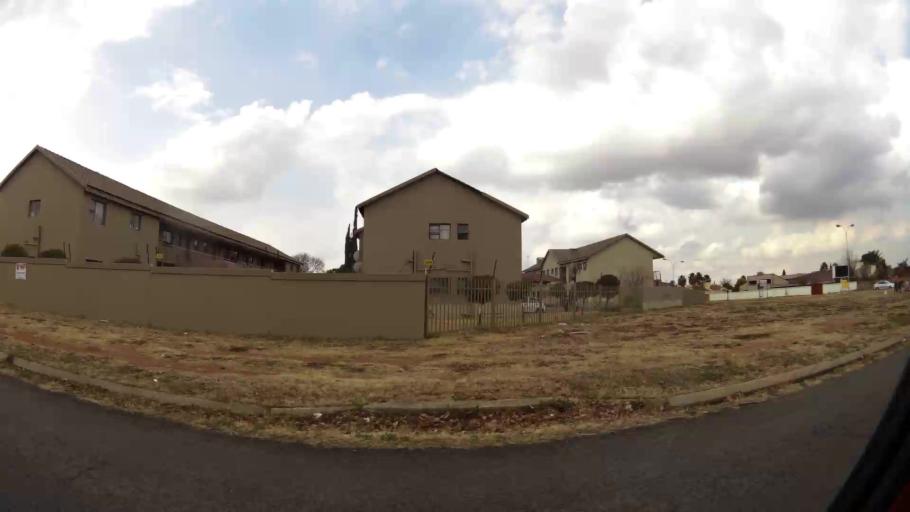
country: ZA
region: Gauteng
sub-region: Sedibeng District Municipality
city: Vanderbijlpark
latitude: -26.7302
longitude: 27.8537
